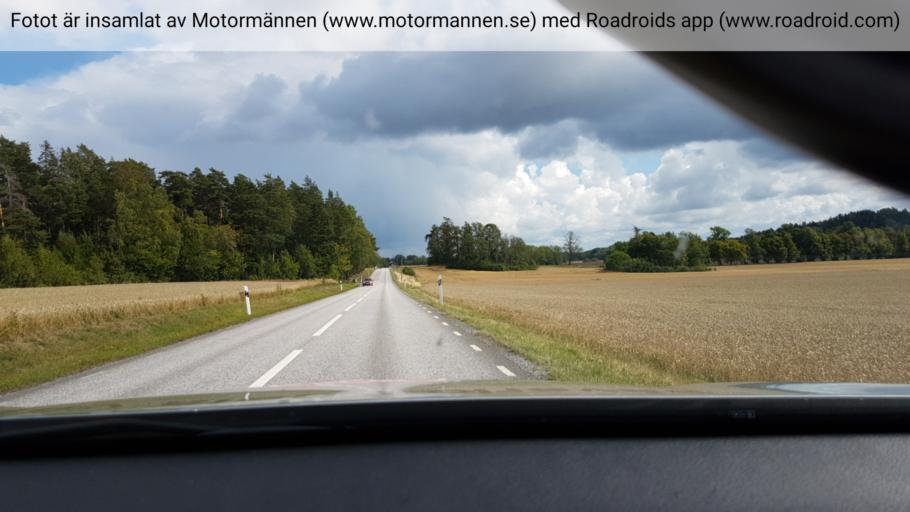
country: SE
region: Stockholm
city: Stenhamra
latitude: 59.2949
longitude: 17.6780
